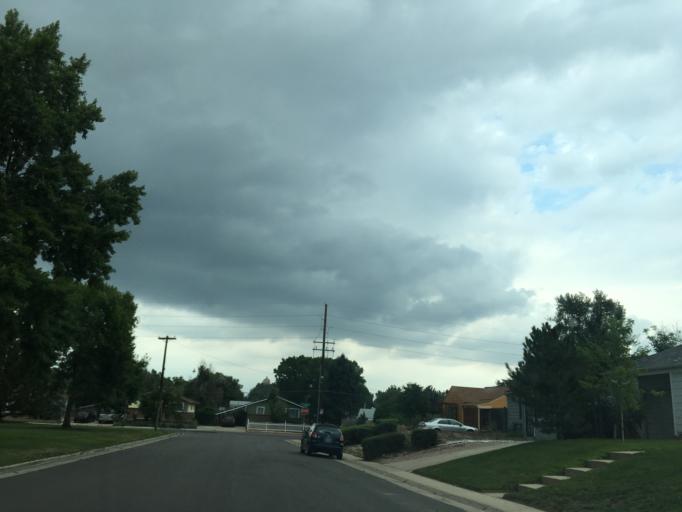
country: US
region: Colorado
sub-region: Arapahoe County
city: Sheridan
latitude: 39.6888
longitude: -105.0089
